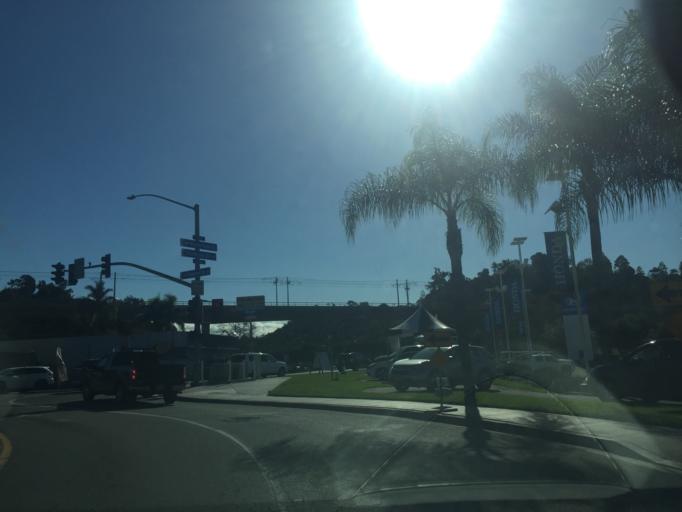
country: US
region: California
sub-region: San Diego County
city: La Mesa
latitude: 32.7815
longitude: -117.1016
